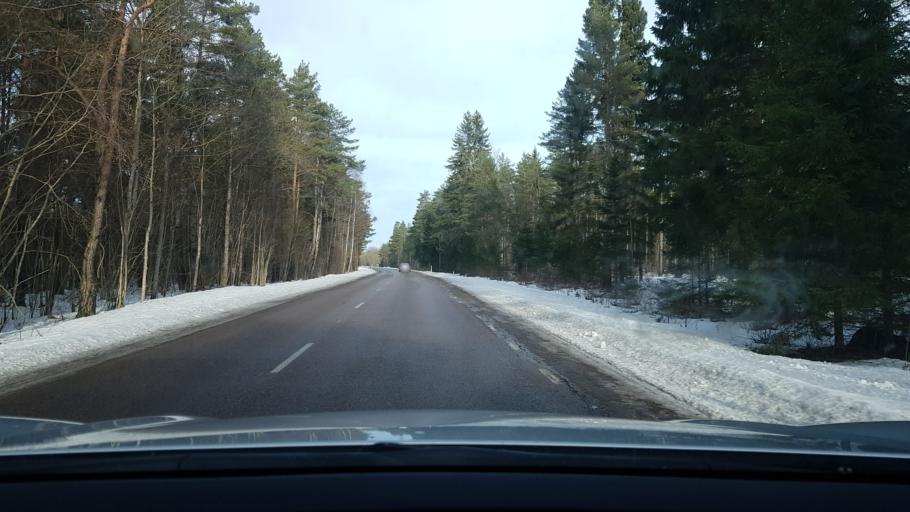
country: EE
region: Saare
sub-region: Kuressaare linn
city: Kuressaare
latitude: 58.3669
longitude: 22.6166
